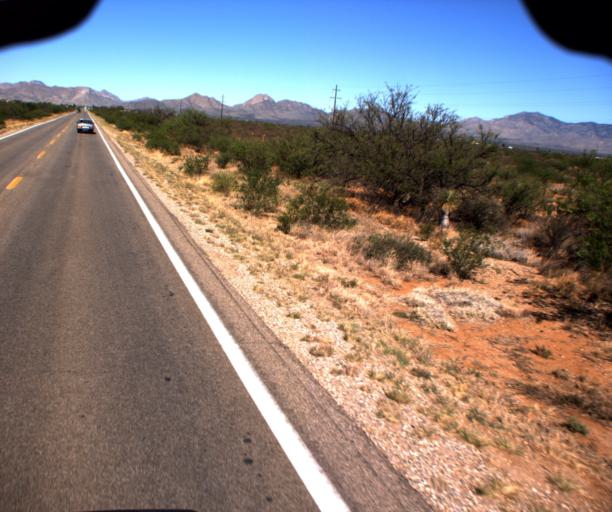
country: US
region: Arizona
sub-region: Cochise County
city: Huachuca City
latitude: 31.6934
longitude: -110.3194
